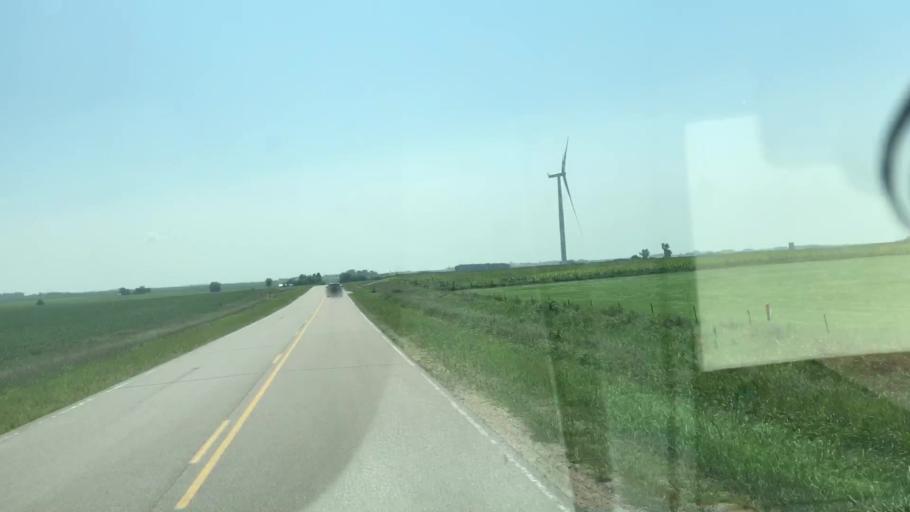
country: US
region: Iowa
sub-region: O'Brien County
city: Sanborn
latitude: 43.2004
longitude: -95.7231
